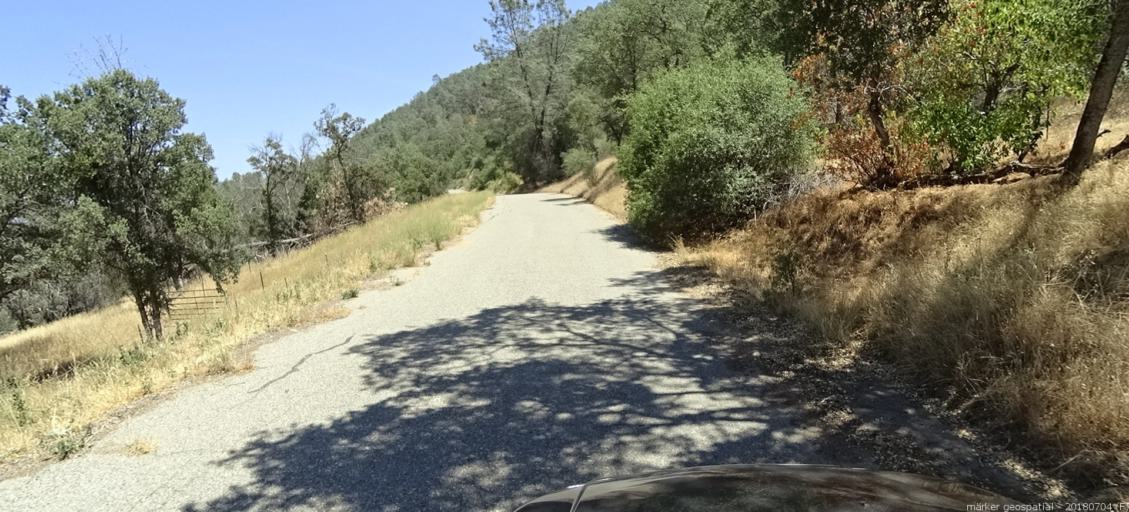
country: US
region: California
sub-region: Madera County
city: Coarsegold
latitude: 37.1813
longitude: -119.6148
